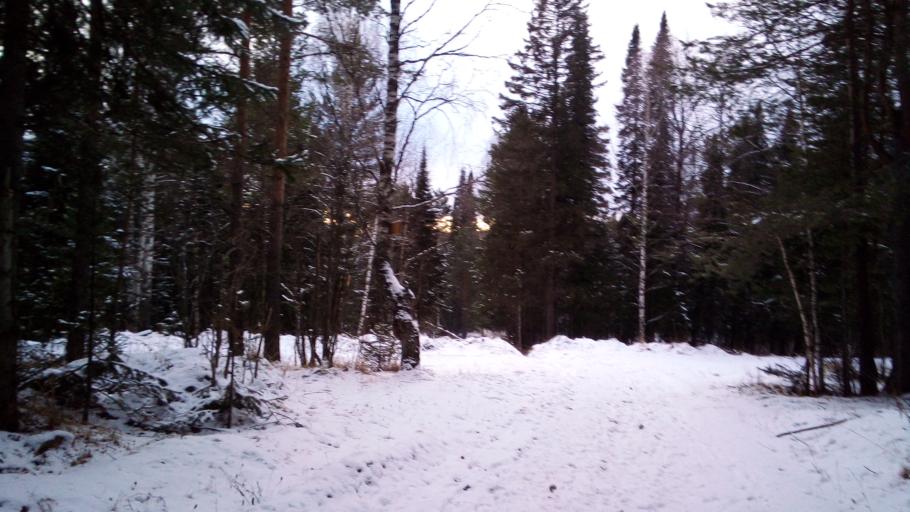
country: RU
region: Chelyabinsk
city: Satka
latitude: 54.8171
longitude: 59.0046
